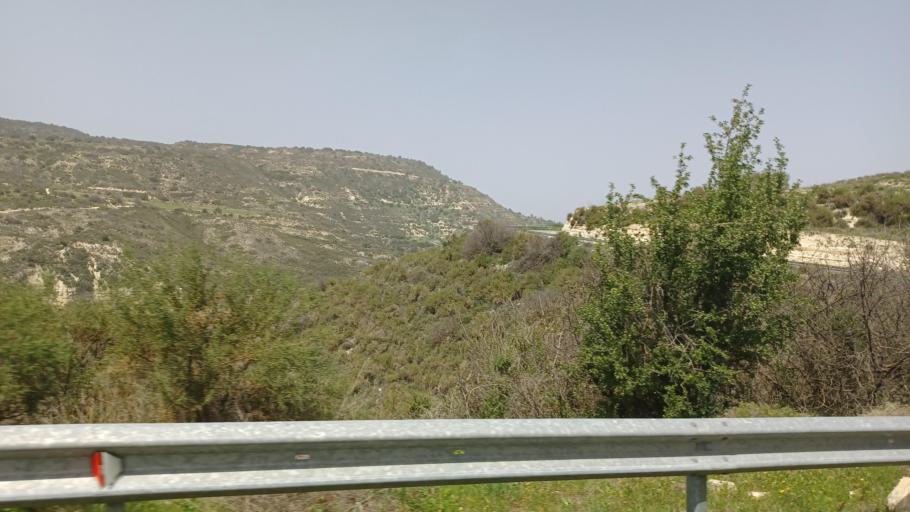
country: CY
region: Limassol
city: Pachna
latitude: 34.7616
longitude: 32.7453
